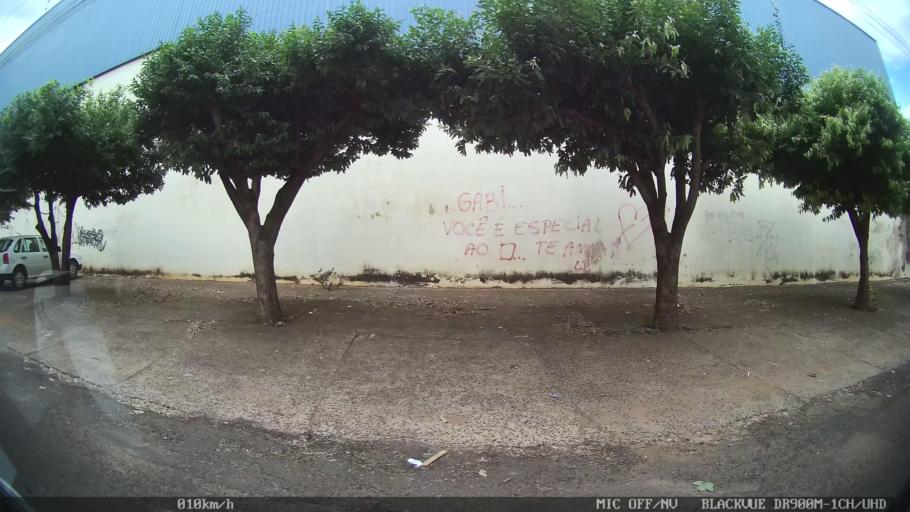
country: BR
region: Sao Paulo
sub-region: Sao Jose Do Rio Preto
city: Sao Jose do Rio Preto
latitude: -20.8099
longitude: -49.4995
